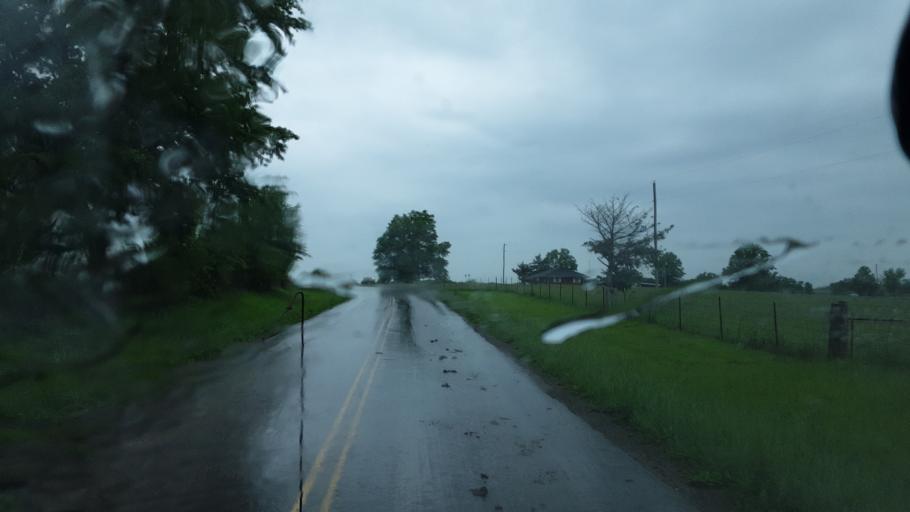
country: US
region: Missouri
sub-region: Randolph County
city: Moberly
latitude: 39.3684
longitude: -92.2653
